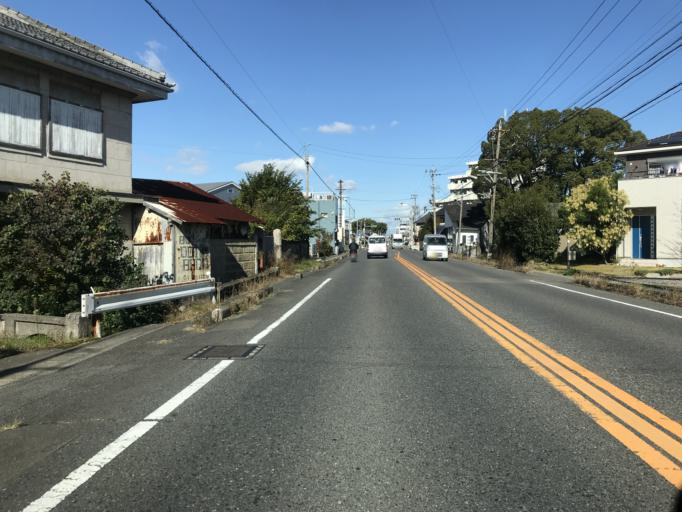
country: JP
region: Aichi
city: Inazawa
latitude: 35.2242
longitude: 136.8408
